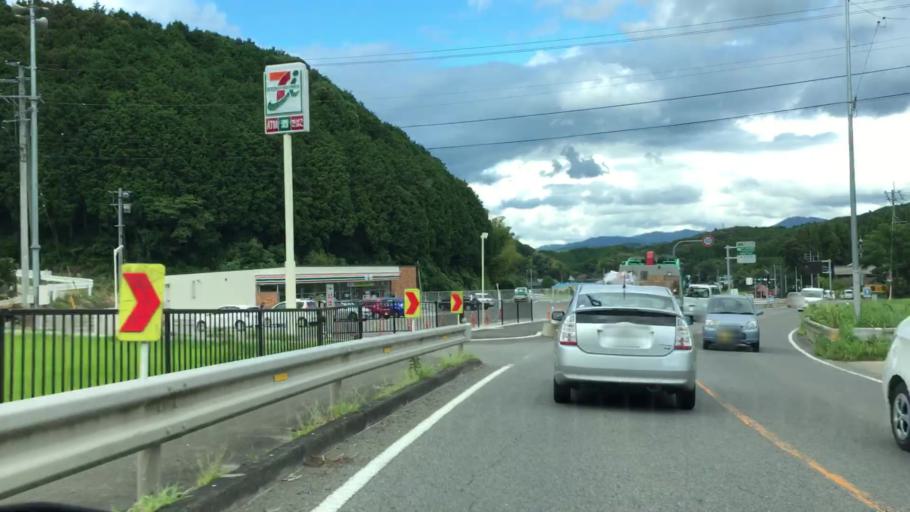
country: JP
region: Saga Prefecture
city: Imaricho-ko
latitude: 33.2928
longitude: 129.9099
